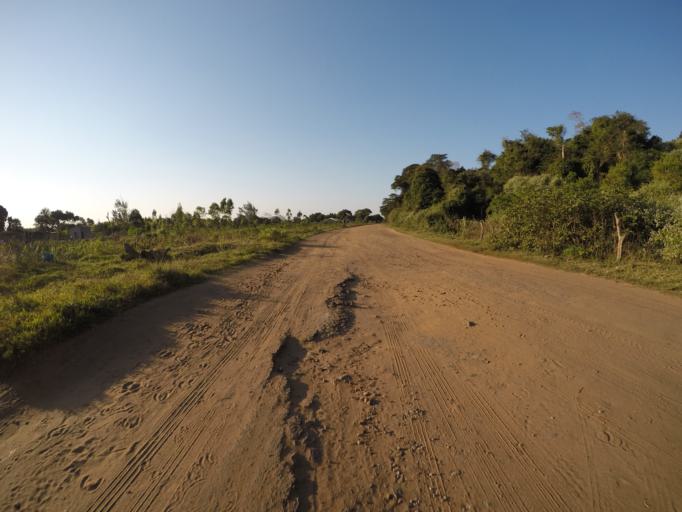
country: ZA
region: KwaZulu-Natal
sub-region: uThungulu District Municipality
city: KwaMbonambi
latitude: -28.7073
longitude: 32.1850
